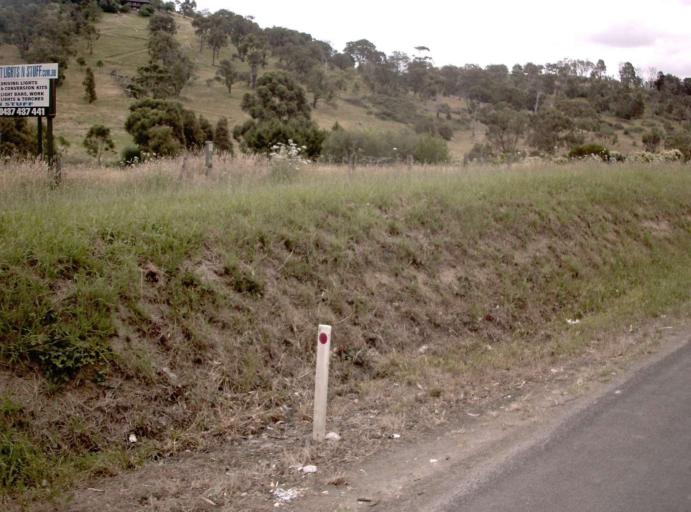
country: AU
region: Victoria
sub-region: Yarra Ranges
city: Lilydale
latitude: -37.7460
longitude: 145.3738
